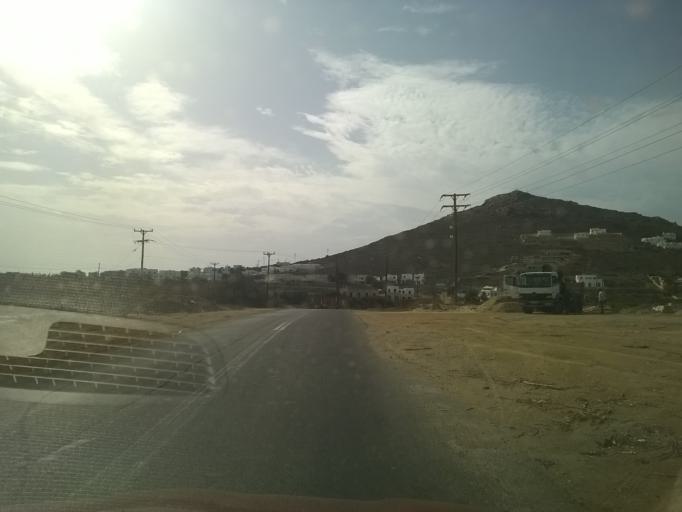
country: GR
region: South Aegean
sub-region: Nomos Kykladon
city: Naxos
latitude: 37.0860
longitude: 25.3528
